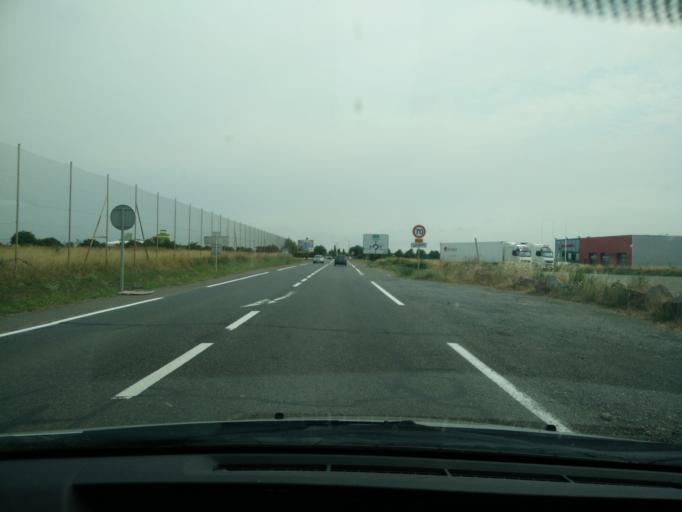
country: FR
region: Poitou-Charentes
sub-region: Departement des Deux-Sevres
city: Thouars
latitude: 46.9871
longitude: -0.1977
